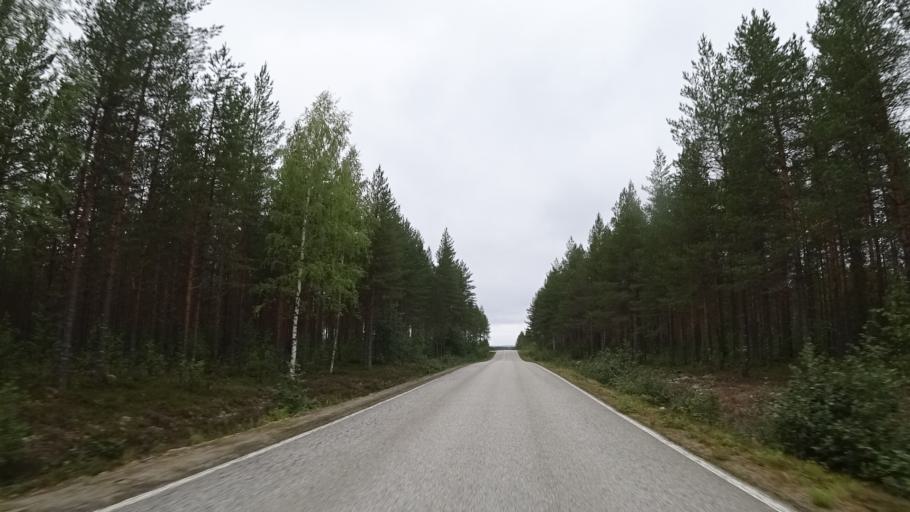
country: FI
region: North Karelia
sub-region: Pielisen Karjala
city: Lieksa
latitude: 63.3627
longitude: 30.2830
